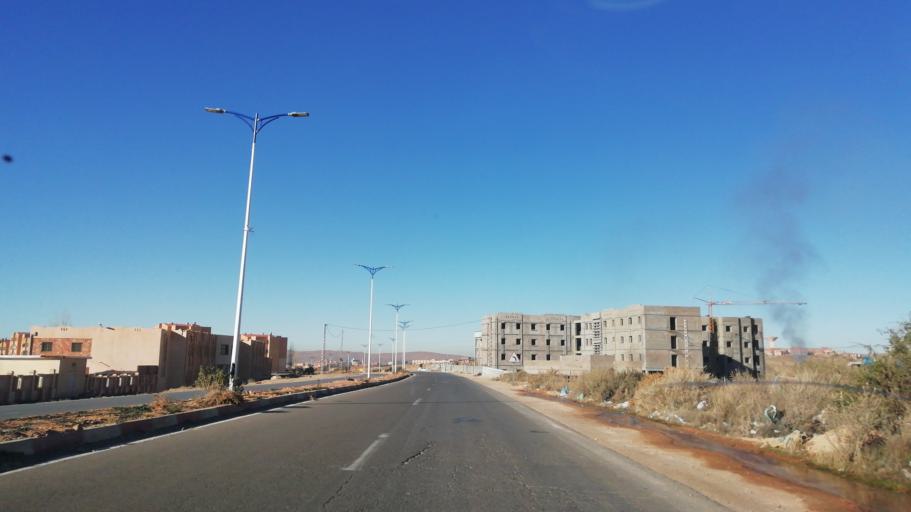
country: DZ
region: El Bayadh
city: El Bayadh
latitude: 33.6878
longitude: 1.0426
